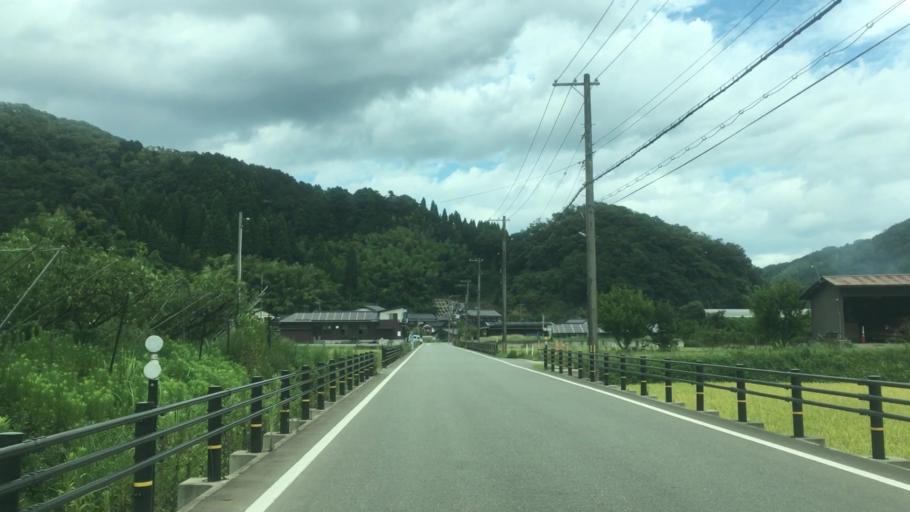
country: JP
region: Hyogo
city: Toyooka
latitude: 35.5915
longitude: 134.7983
